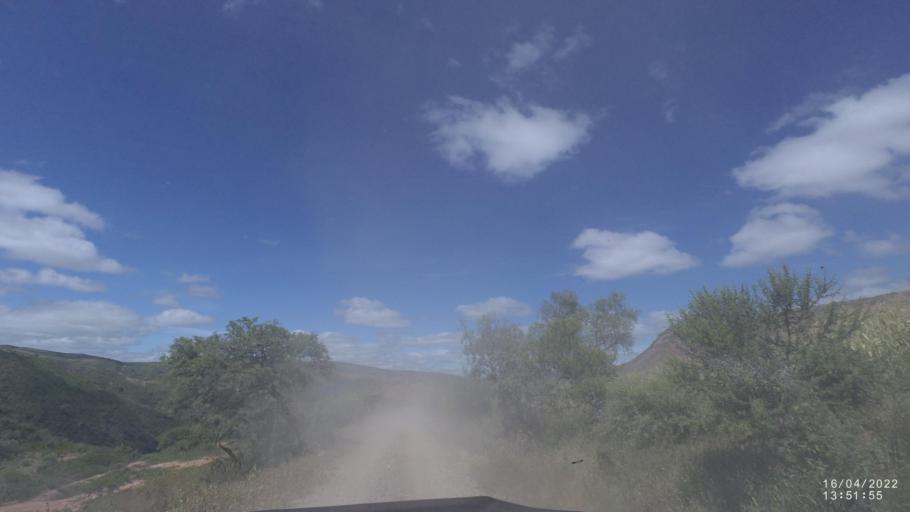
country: BO
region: Cochabamba
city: Mizque
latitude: -18.0206
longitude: -65.5736
